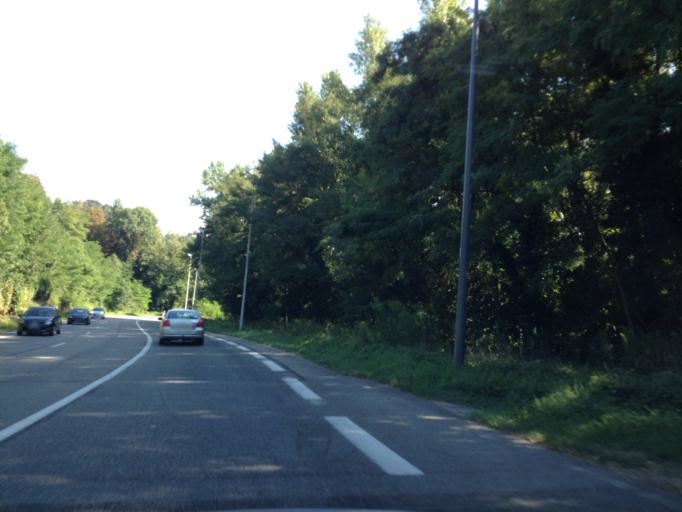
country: FR
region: Rhone-Alpes
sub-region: Departement de la Savoie
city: La Motte-Servolex
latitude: 45.5920
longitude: 5.9060
